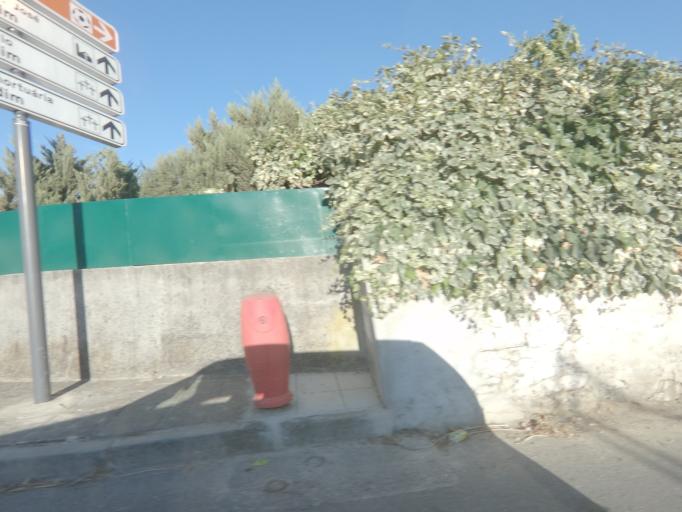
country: PT
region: Vila Real
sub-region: Peso da Regua
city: Godim
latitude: 41.1696
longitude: -7.8015
